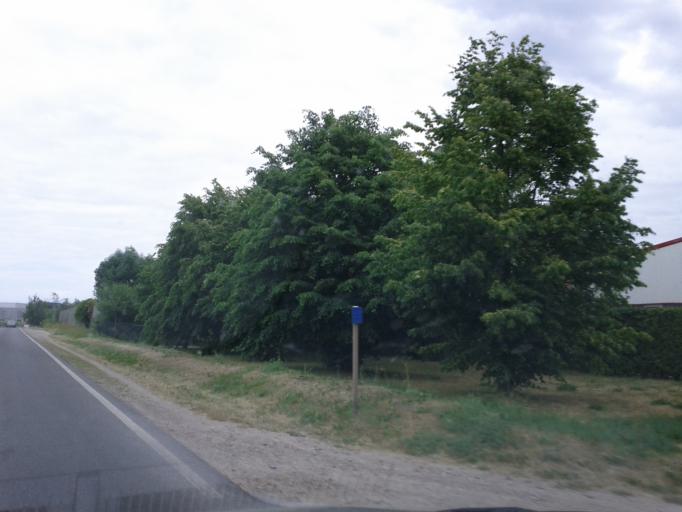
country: DE
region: Brandenburg
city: Hoppegarten
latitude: 52.5038
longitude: 13.6442
